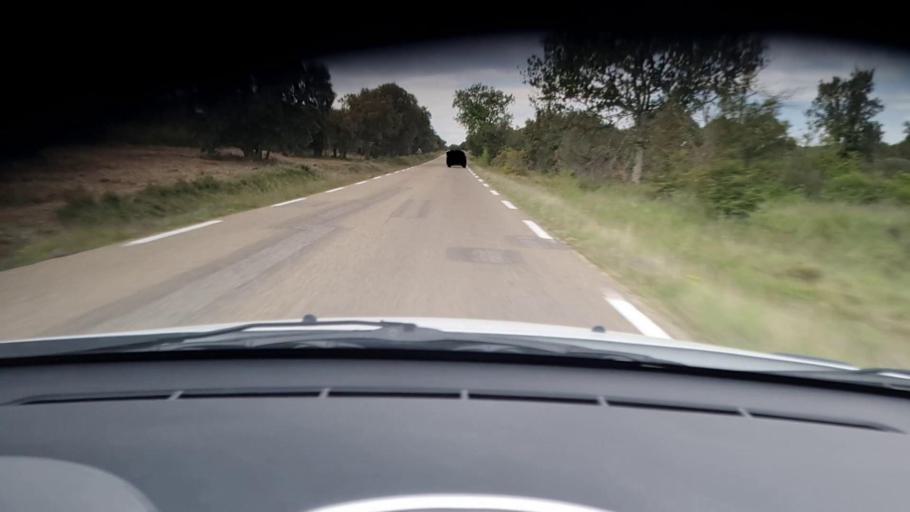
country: FR
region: Languedoc-Roussillon
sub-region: Departement du Gard
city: Blauzac
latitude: 43.9766
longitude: 4.4031
